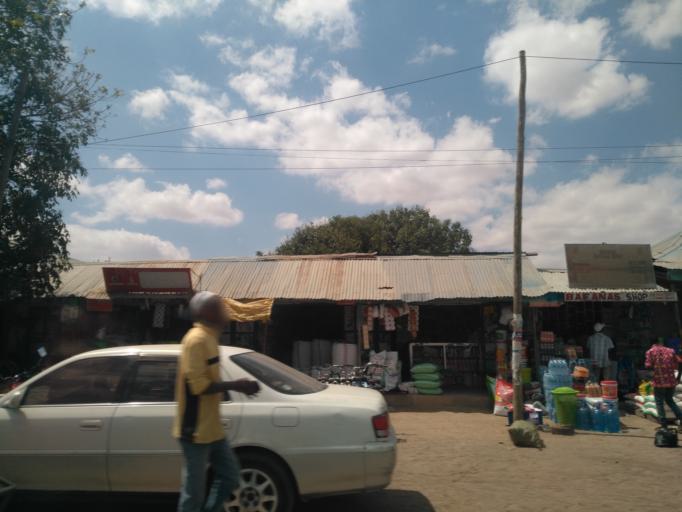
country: TZ
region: Dodoma
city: Dodoma
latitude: -6.1788
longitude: 35.7419
